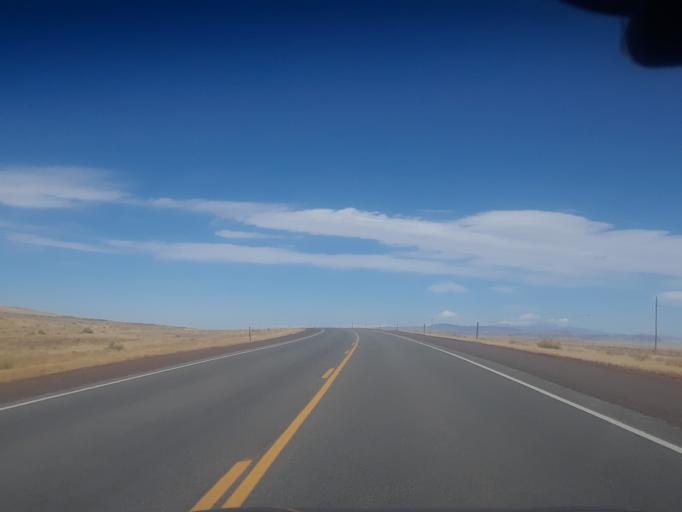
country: US
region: Colorado
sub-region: Conejos County
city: Conejos
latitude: 36.8332
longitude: -105.9741
